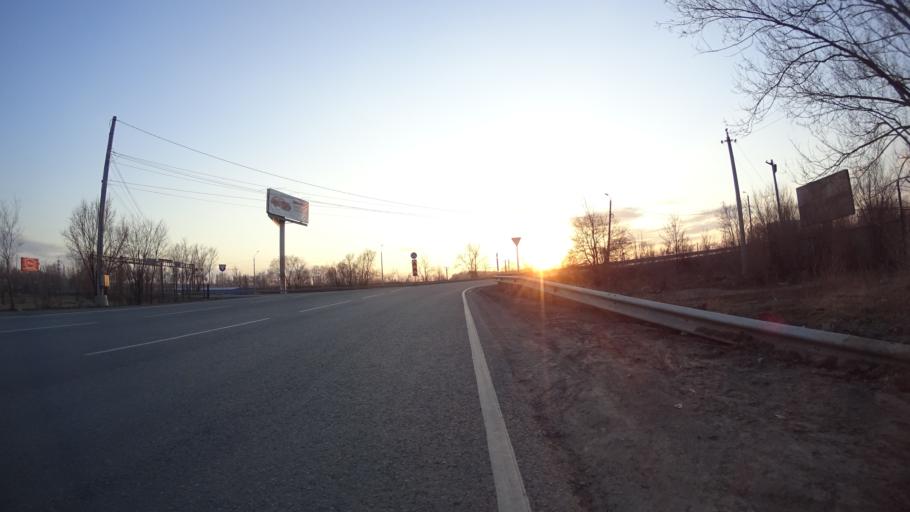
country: RU
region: Chelyabinsk
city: Novosineglazovskiy
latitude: 55.0792
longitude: 61.3895
